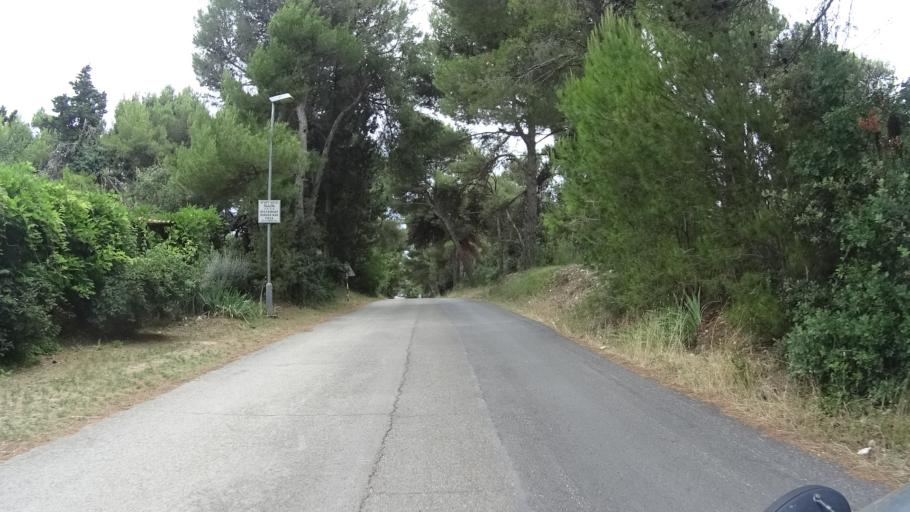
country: HR
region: Istarska
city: Medulin
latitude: 44.8046
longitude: 13.9074
